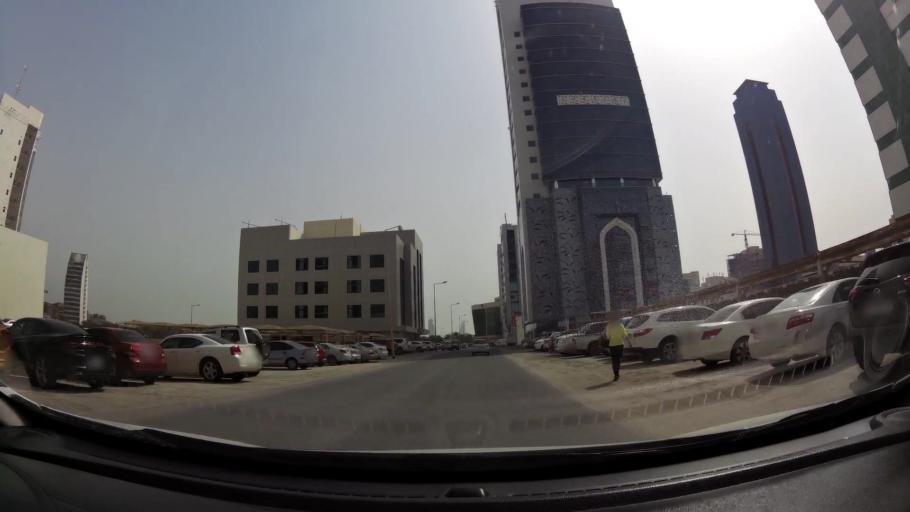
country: BH
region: Manama
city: Jidd Hafs
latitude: 26.2378
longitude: 50.5392
